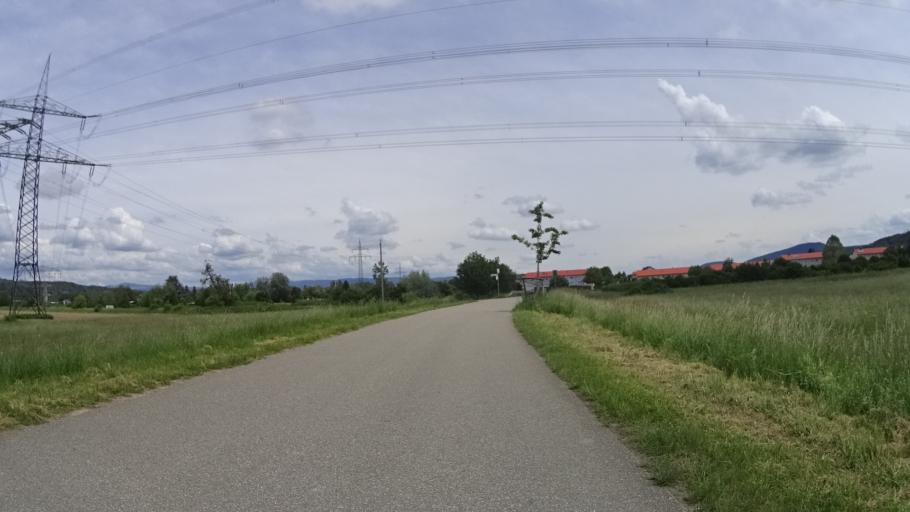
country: DE
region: Baden-Wuerttemberg
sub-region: Freiburg Region
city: Rheinfelden (Baden)
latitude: 47.5550
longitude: 7.7559
